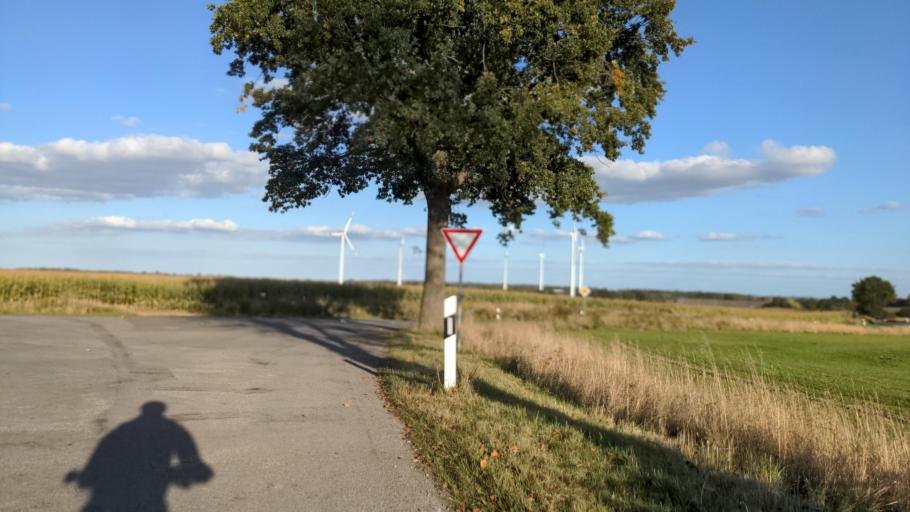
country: DE
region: Schleswig-Holstein
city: Strukdorf
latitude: 53.9560
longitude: 10.5284
